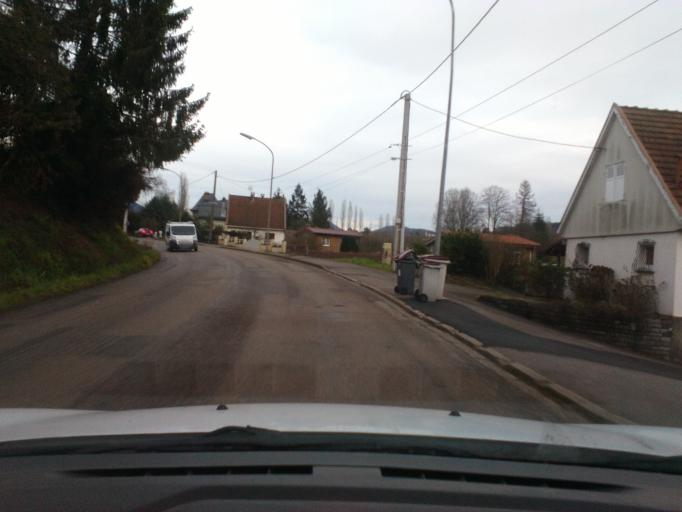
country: FR
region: Lorraine
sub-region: Departement des Vosges
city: Senones
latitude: 48.3933
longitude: 6.9685
